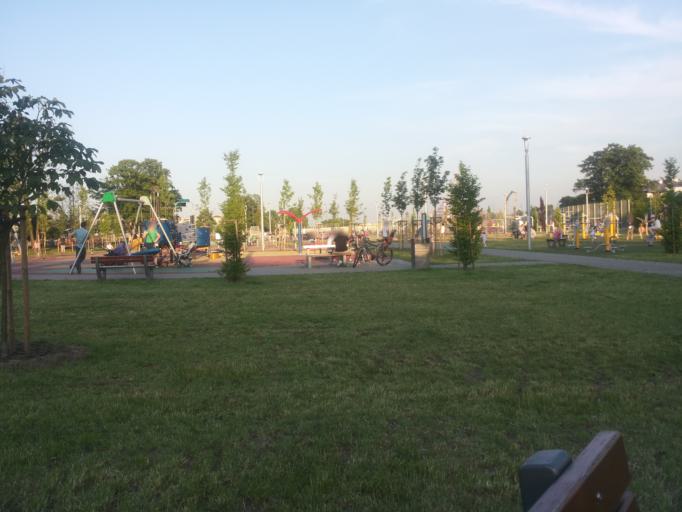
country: PL
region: Masovian Voivodeship
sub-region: Warszawa
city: Targowek
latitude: 52.3127
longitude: 21.0579
